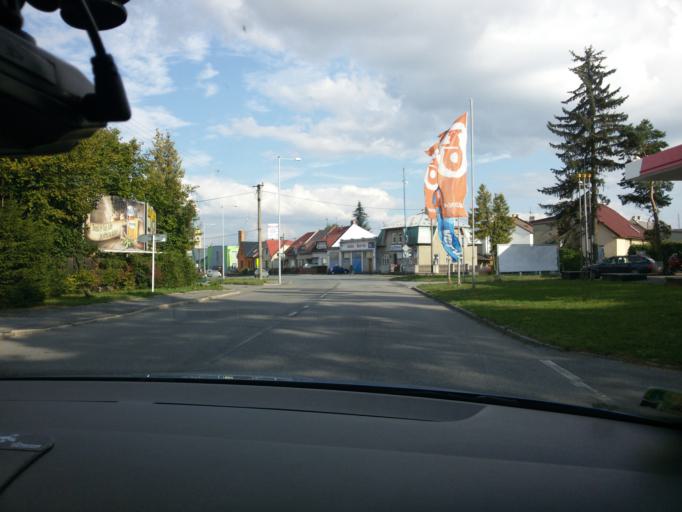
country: CZ
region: Pardubicky
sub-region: Okres Svitavy
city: Policka
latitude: 49.7147
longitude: 16.2566
